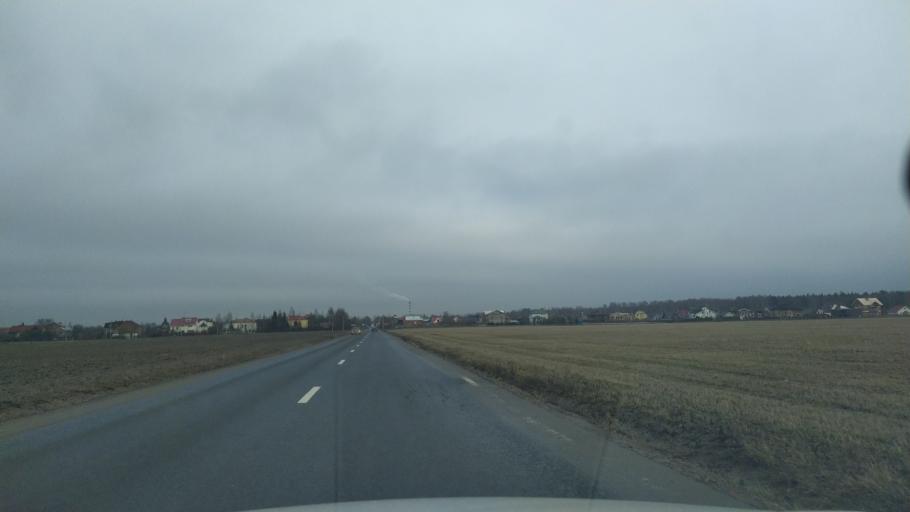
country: RU
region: St.-Petersburg
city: Aleksandrovskaya
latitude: 59.7193
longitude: 30.3418
